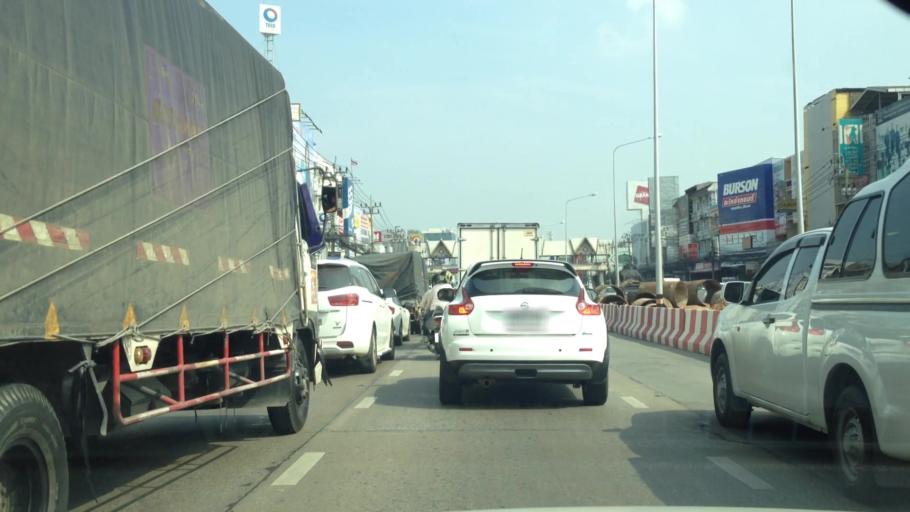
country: TH
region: Bangkok
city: Bang Na
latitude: 13.6404
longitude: 100.6343
